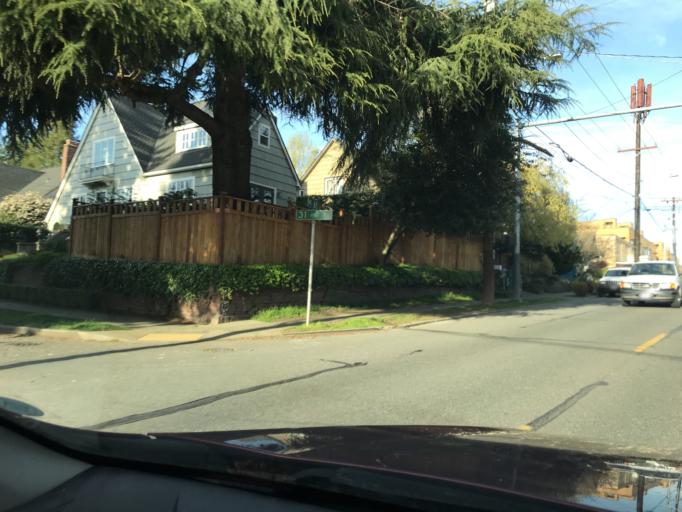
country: US
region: Washington
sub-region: King County
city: Inglewood-Finn Hill
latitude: 47.6758
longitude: -122.2943
